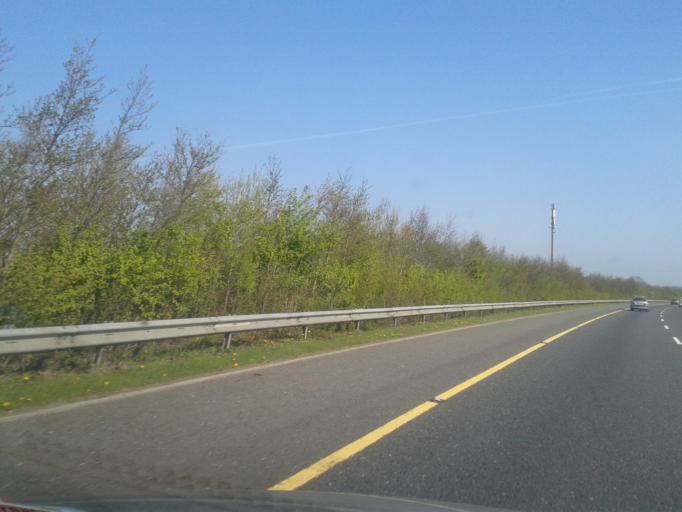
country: IE
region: Leinster
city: Lusk
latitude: 53.5194
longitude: -6.2086
